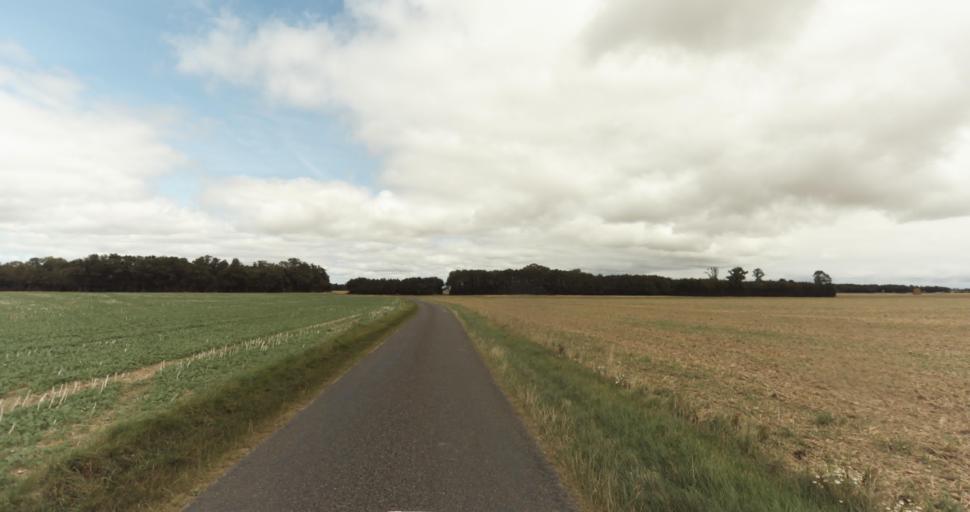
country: FR
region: Haute-Normandie
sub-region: Departement de l'Eure
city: La Madeleine-de-Nonancourt
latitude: 48.8967
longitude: 1.1995
